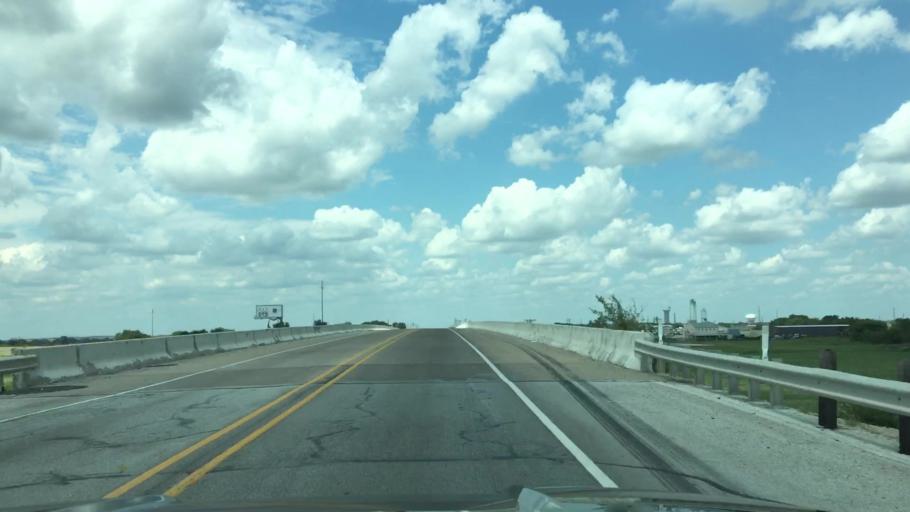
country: US
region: Texas
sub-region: Tarrant County
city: Eagle Mountain
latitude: 32.9436
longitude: -97.4208
